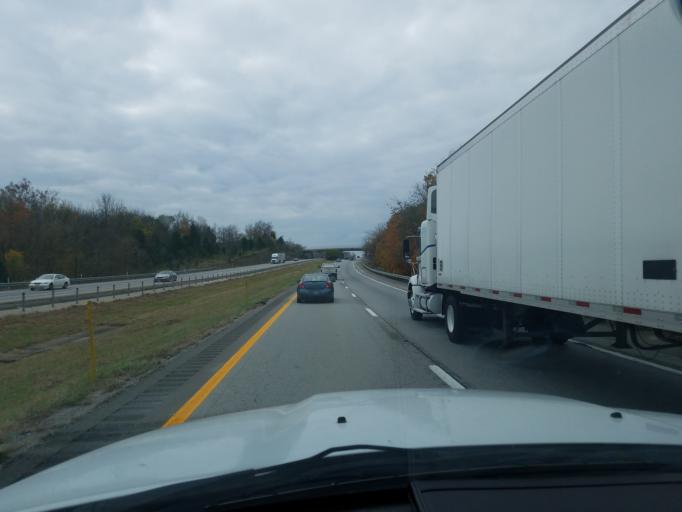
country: US
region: Kentucky
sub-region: Oldham County
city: La Grange
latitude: 38.4379
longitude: -85.3114
